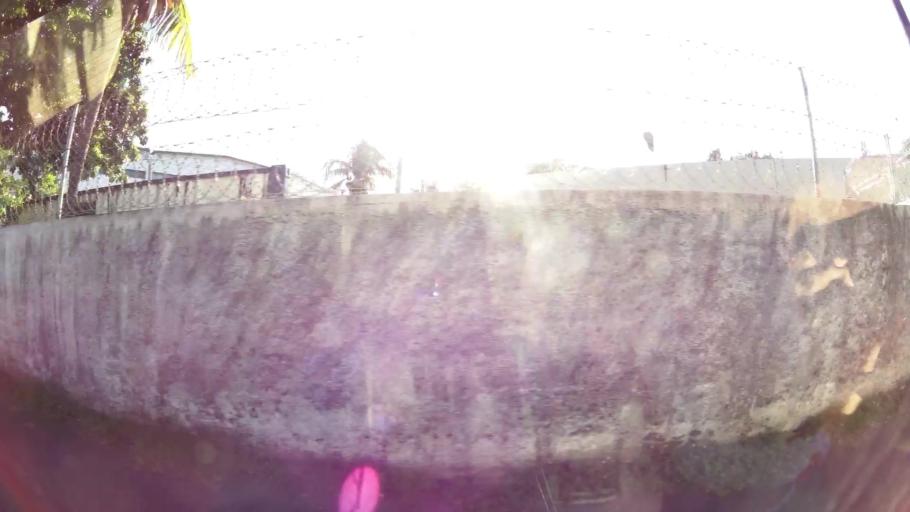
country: MU
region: Port Louis
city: Port Louis
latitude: -20.1546
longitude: 57.5012
